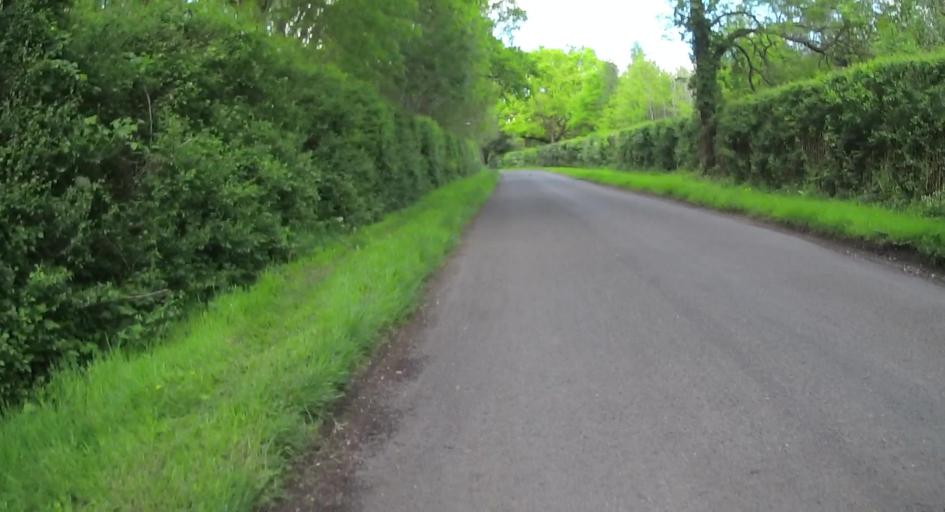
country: GB
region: England
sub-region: West Berkshire
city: Stratfield Mortimer
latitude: 51.3502
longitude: -1.0070
